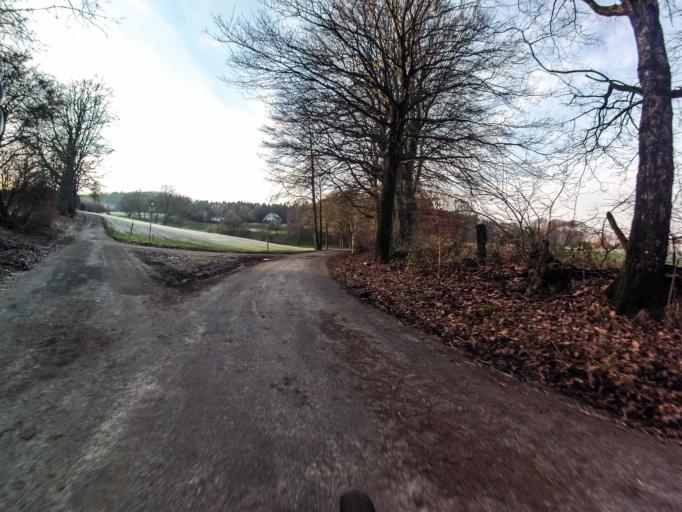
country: DE
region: North Rhine-Westphalia
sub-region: Regierungsbezirk Munster
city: Mettingen
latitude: 52.2870
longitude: 7.7988
